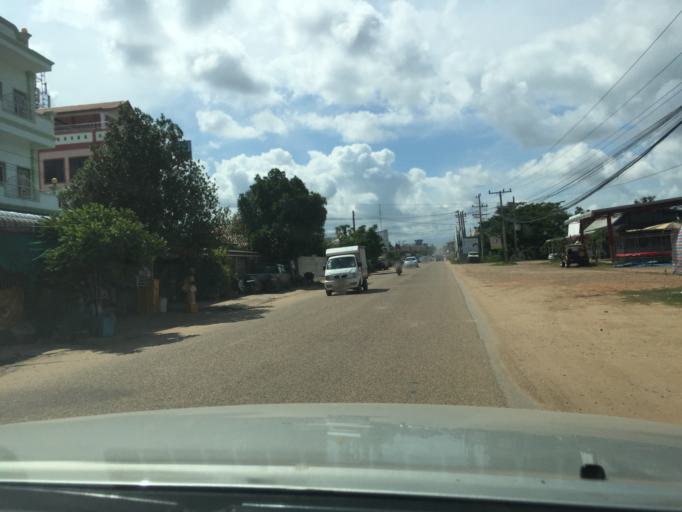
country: LA
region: Savannahkhet
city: Savannakhet
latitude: 16.5494
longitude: 104.7496
